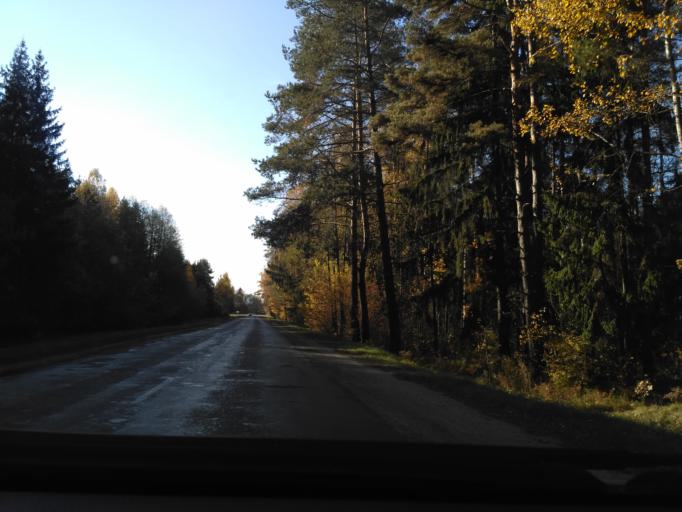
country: BY
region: Minsk
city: Horad Barysaw
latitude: 54.2590
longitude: 28.5768
